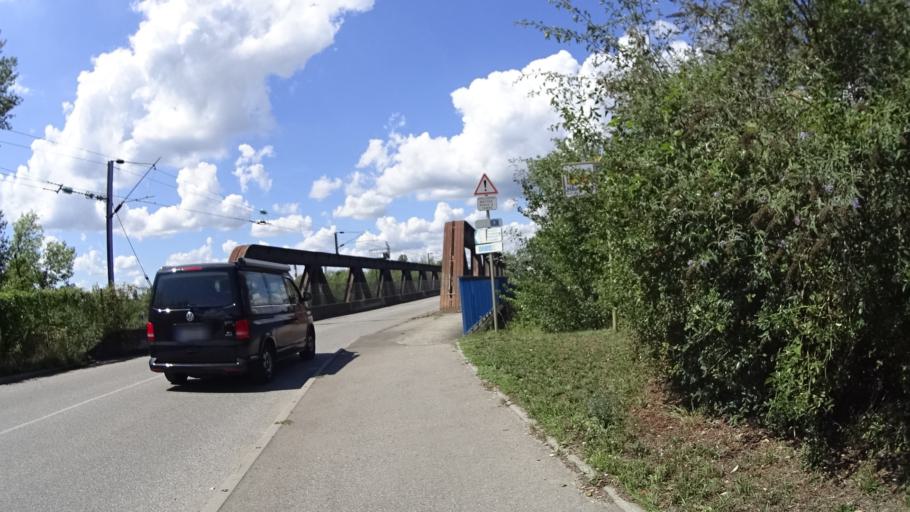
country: FR
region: Alsace
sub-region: Departement du Haut-Rhin
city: Chalampe
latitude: 47.8148
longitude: 7.5442
